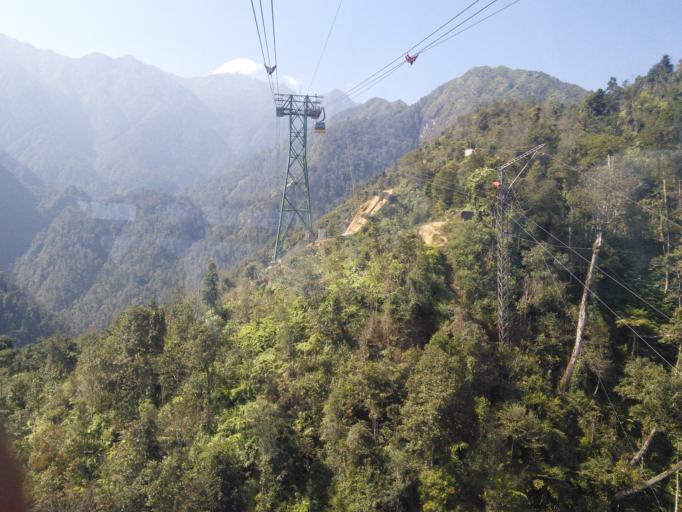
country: VN
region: Lao Cai
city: Sa Pa
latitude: 22.3306
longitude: 103.8139
